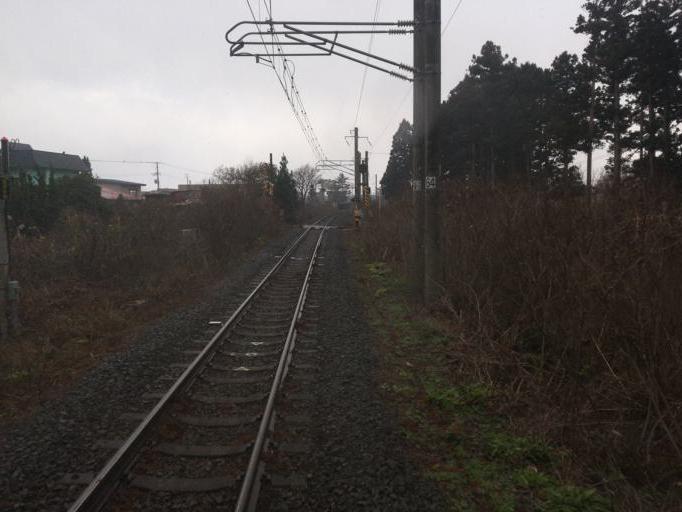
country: JP
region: Aomori
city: Aomori Shi
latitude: 40.9839
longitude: 140.6535
